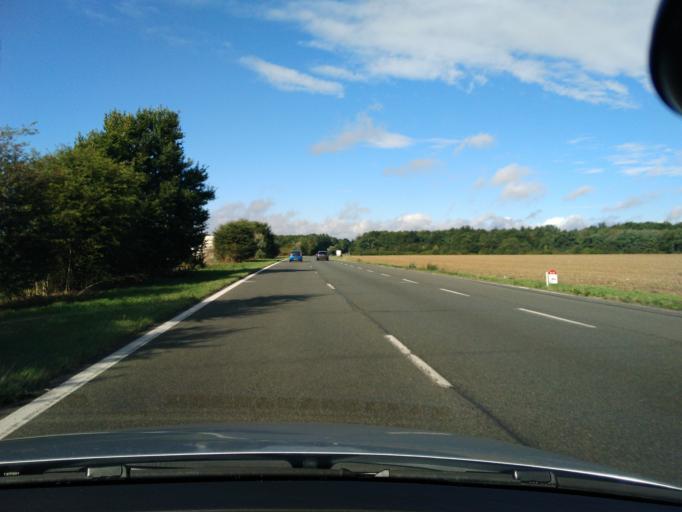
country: FR
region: Haute-Normandie
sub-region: Departement de l'Eure
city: Saint-Germain-sur-Avre
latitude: 48.7494
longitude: 1.2663
